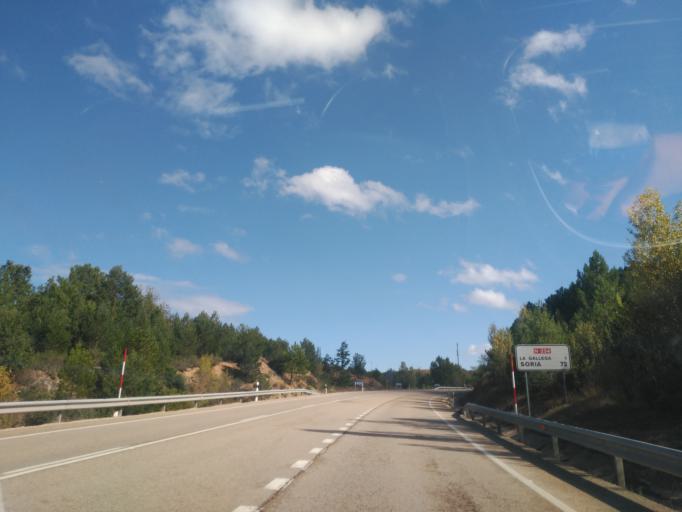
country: ES
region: Castille and Leon
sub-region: Provincia de Burgos
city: Pinilla de los Barruecos
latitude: 41.9033
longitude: -3.2735
